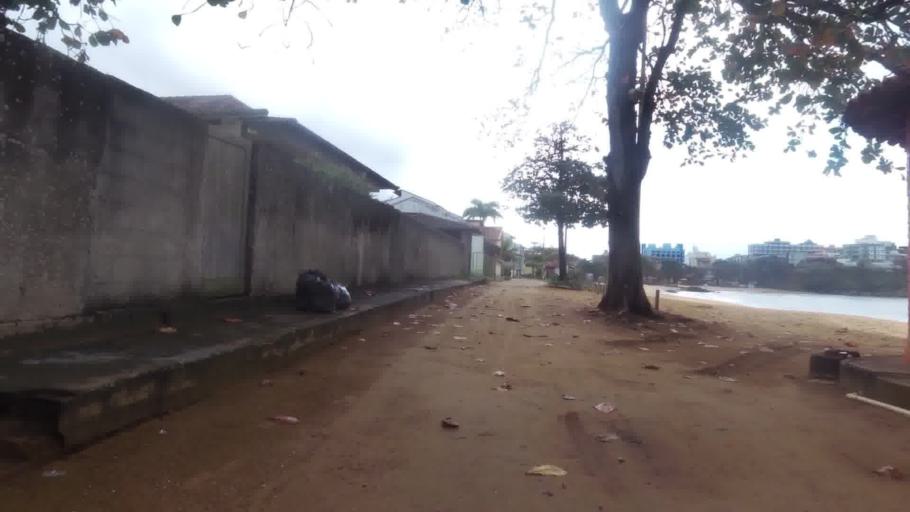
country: BR
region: Espirito Santo
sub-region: Piuma
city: Piuma
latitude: -20.8337
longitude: -40.6997
